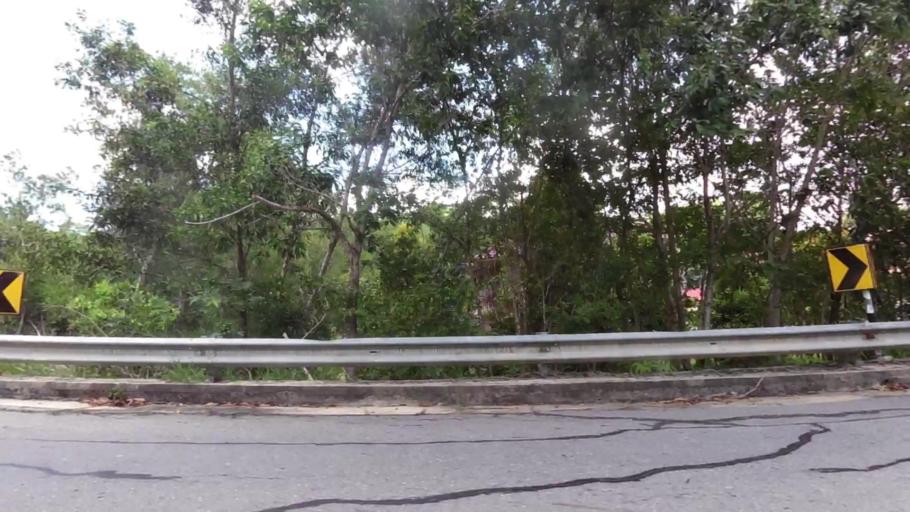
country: BN
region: Brunei and Muara
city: Bandar Seri Begawan
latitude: 4.9310
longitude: 114.9652
